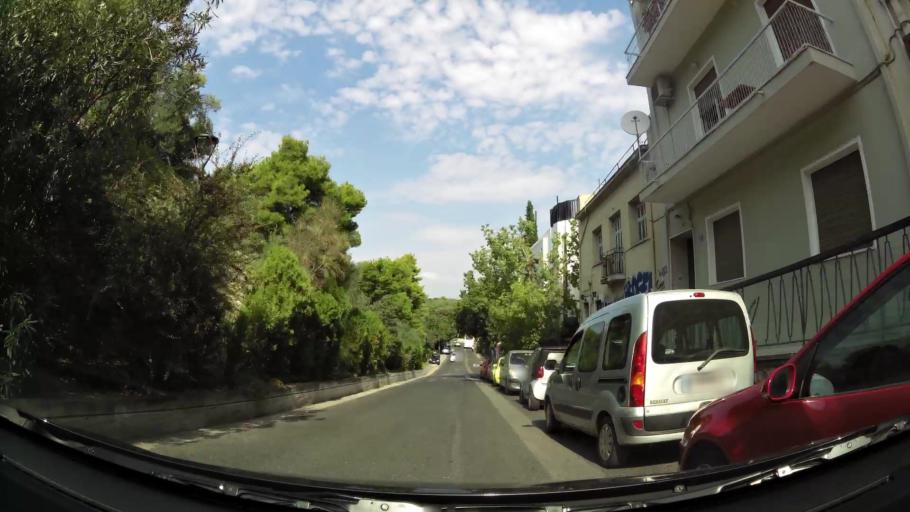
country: GR
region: Attica
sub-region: Nomarchia Athinas
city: Athens
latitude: 37.9683
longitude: 23.7237
